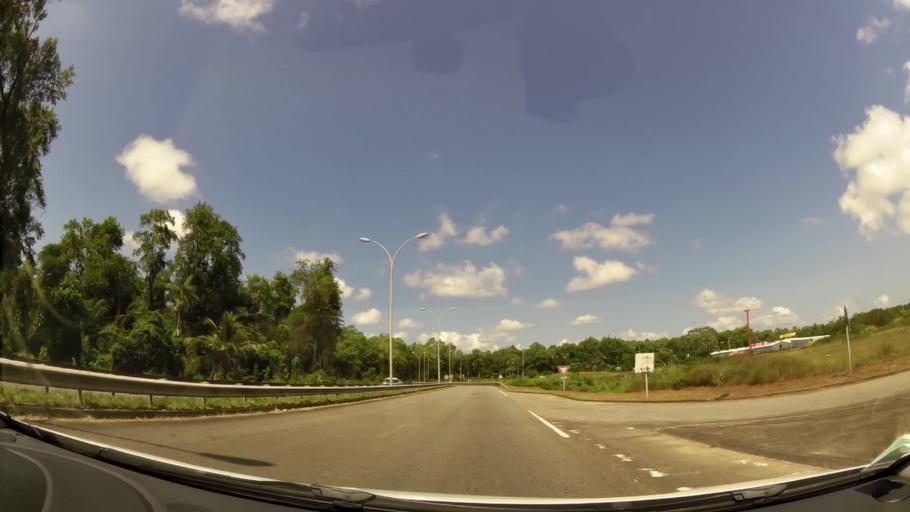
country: GF
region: Guyane
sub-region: Guyane
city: Cayenne
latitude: 4.9220
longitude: -52.3280
